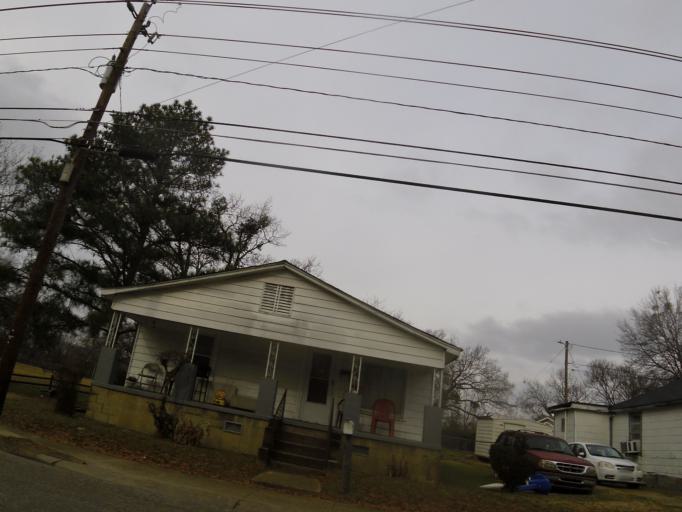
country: US
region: Alabama
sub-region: Montgomery County
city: Montgomery
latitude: 32.4089
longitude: -86.3036
